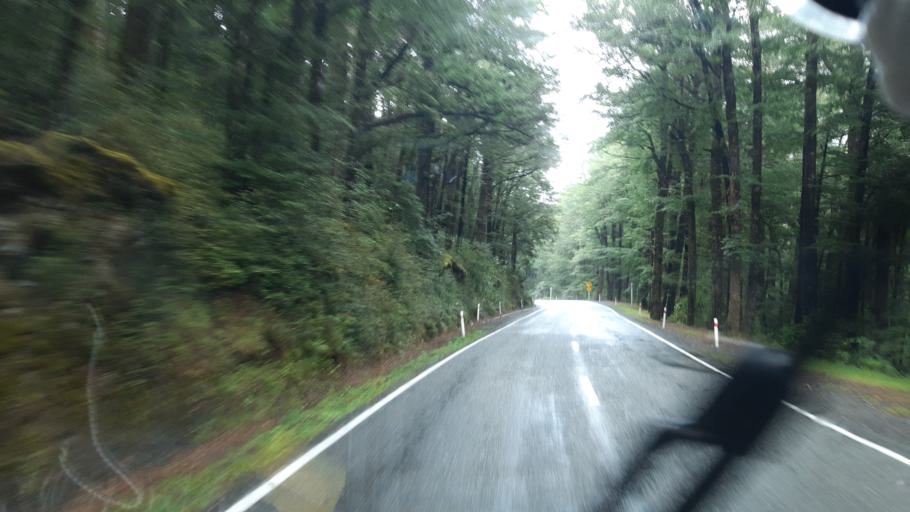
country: NZ
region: Canterbury
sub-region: Hurunui District
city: Amberley
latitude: -42.3775
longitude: 172.3529
